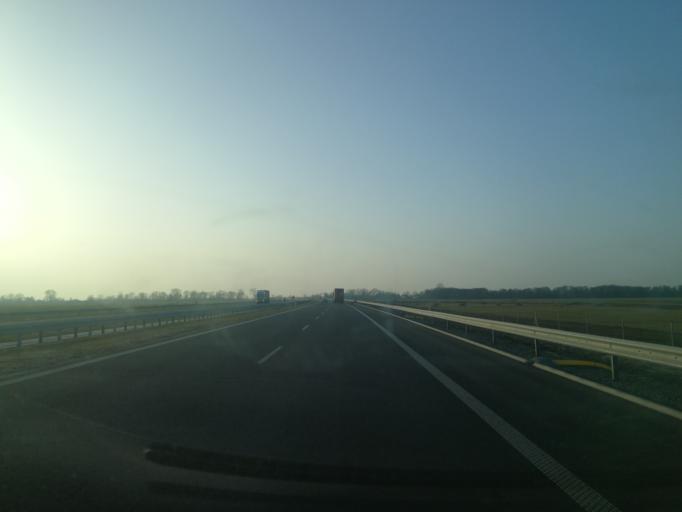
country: PL
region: Pomeranian Voivodeship
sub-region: Powiat nowodworski
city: Nowy Dwor Gdanski
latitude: 54.1714
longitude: 19.2183
